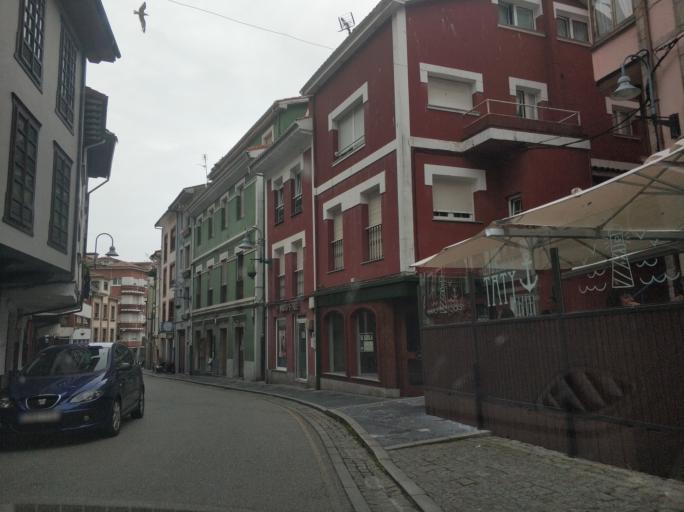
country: ES
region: Asturias
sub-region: Province of Asturias
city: Cudillero
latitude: 43.5619
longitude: -6.1465
